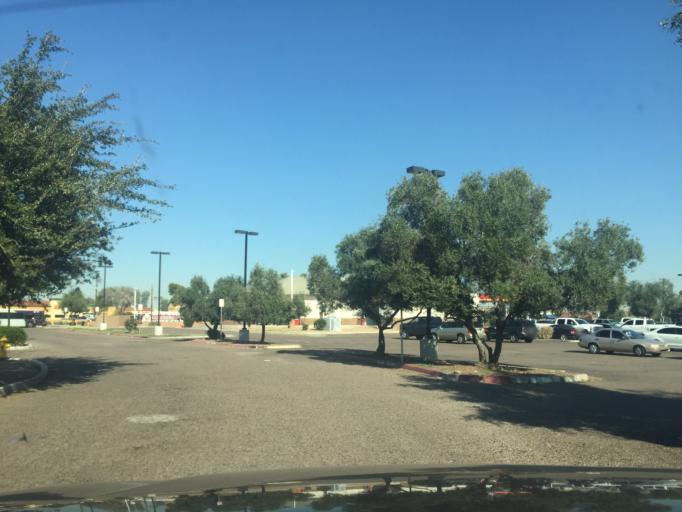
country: US
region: Arizona
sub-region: Maricopa County
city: Tolleson
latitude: 33.4791
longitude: -112.2218
